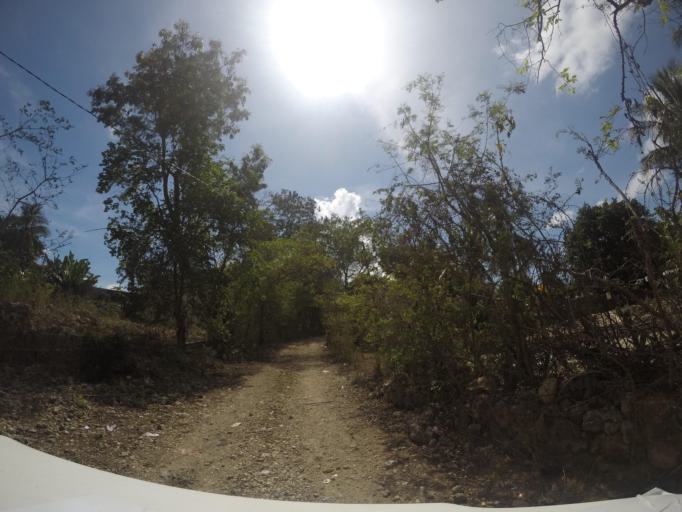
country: TL
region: Baucau
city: Baucau
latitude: -8.4672
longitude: 126.4610
